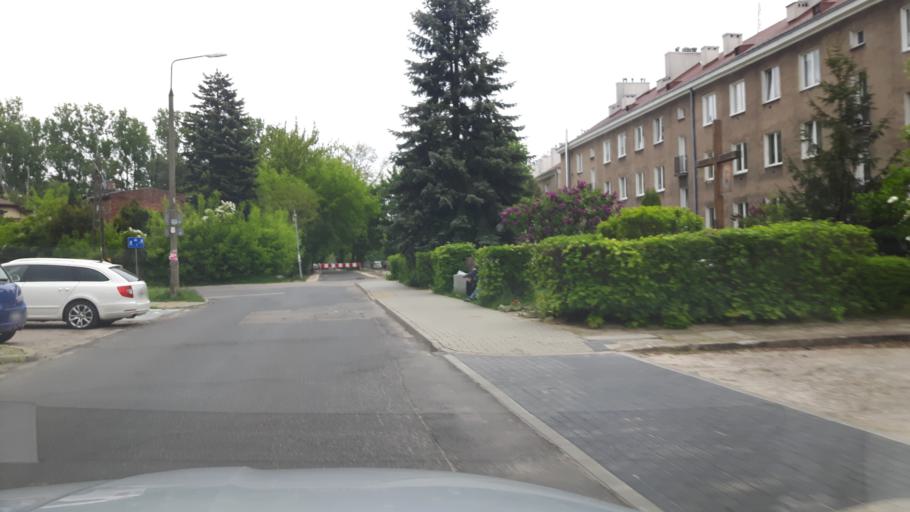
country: PL
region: Masovian Voivodeship
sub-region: Warszawa
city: Rembertow
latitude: 52.2536
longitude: 21.1579
